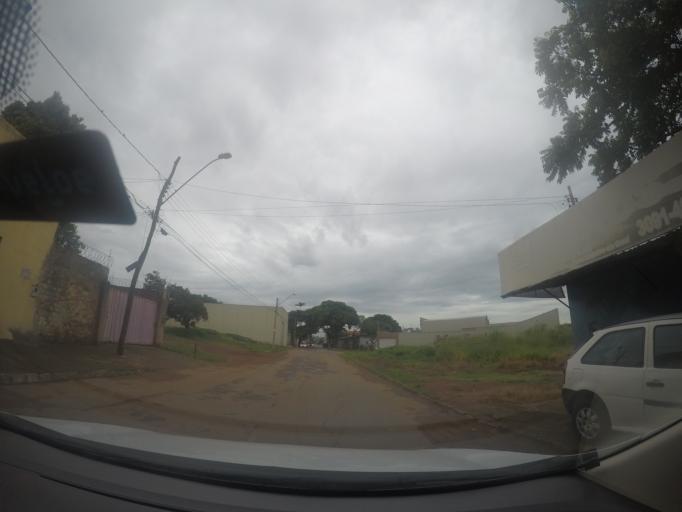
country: BR
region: Goias
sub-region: Goiania
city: Goiania
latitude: -16.6625
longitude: -49.3113
